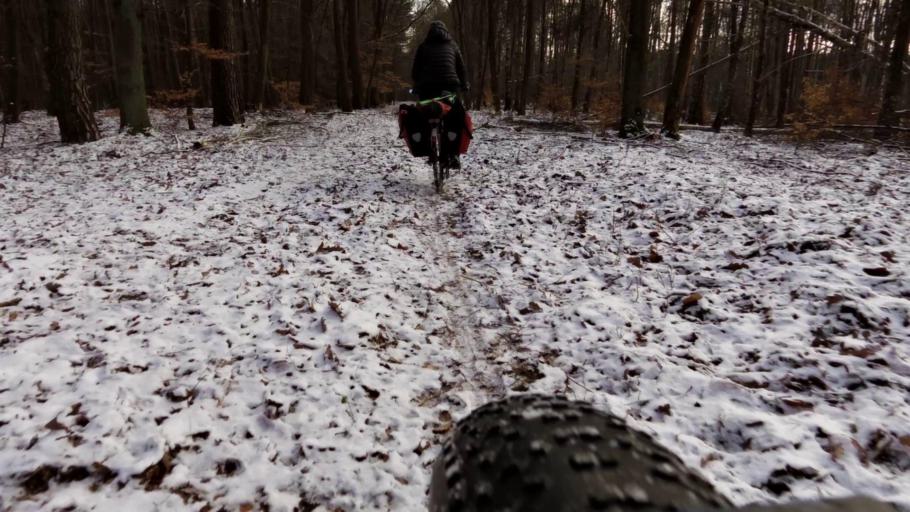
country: PL
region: West Pomeranian Voivodeship
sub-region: Powiat walecki
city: Tuczno
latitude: 53.2983
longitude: 16.2894
